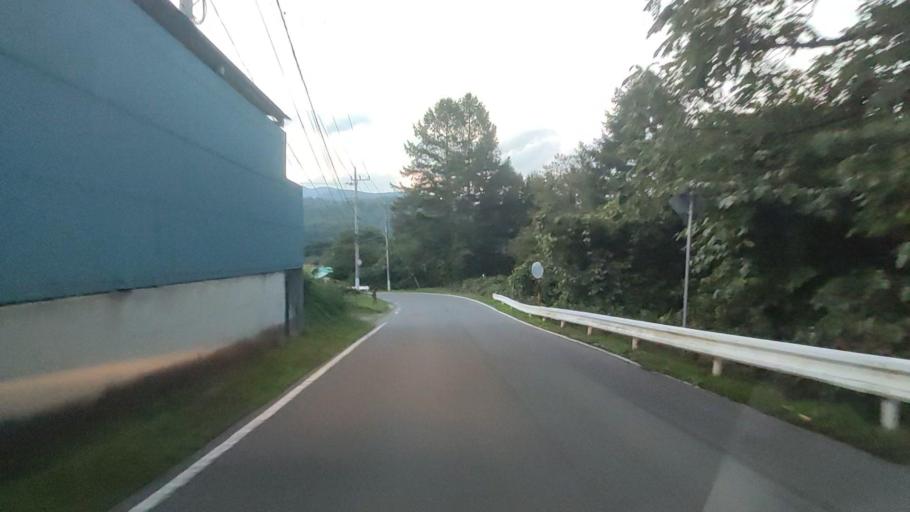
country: JP
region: Gunma
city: Nakanojomachi
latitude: 36.5415
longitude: 138.6030
